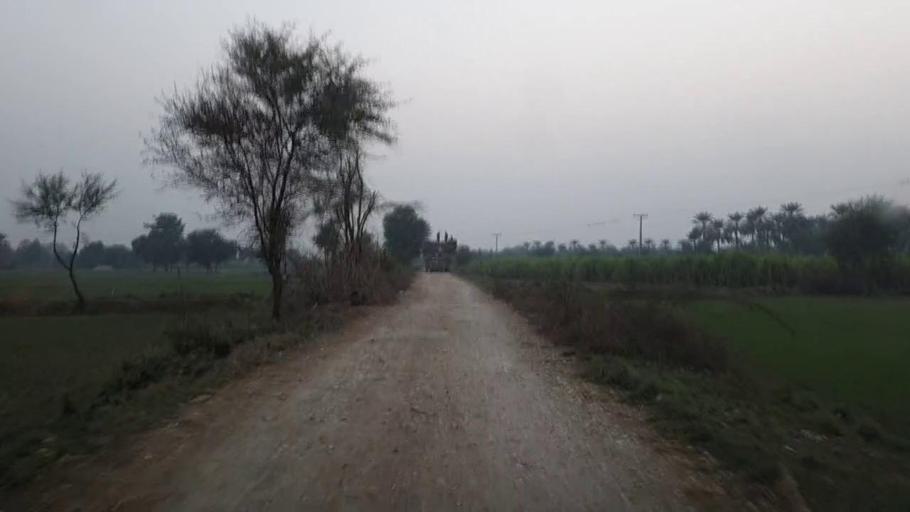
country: PK
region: Sindh
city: Karaundi
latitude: 26.9472
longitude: 68.4477
